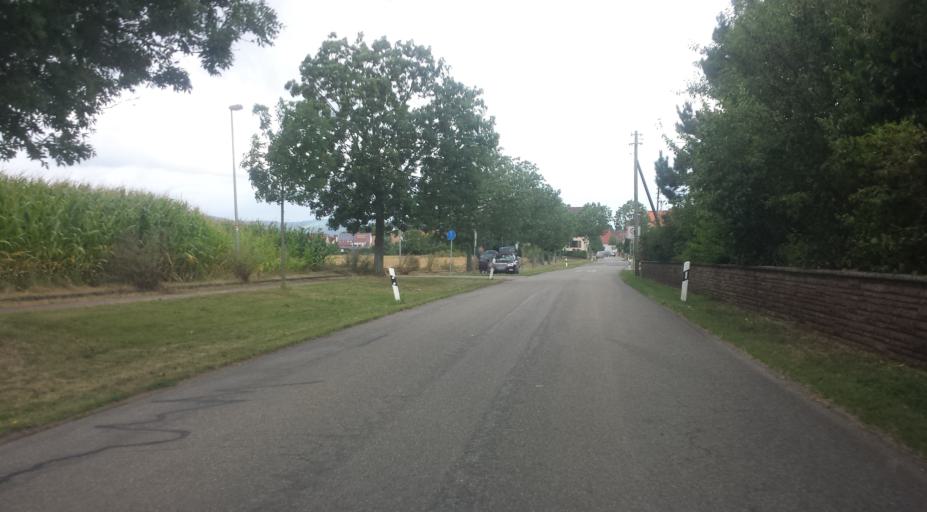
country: DE
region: Rheinland-Pfalz
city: Bornheim
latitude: 49.2145
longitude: 8.1528
